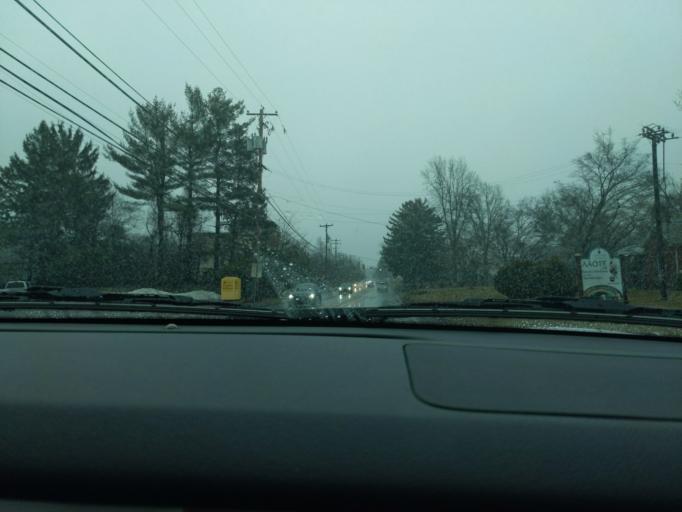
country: US
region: Pennsylvania
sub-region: Bucks County
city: Dublin
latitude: 40.3685
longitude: -75.1978
